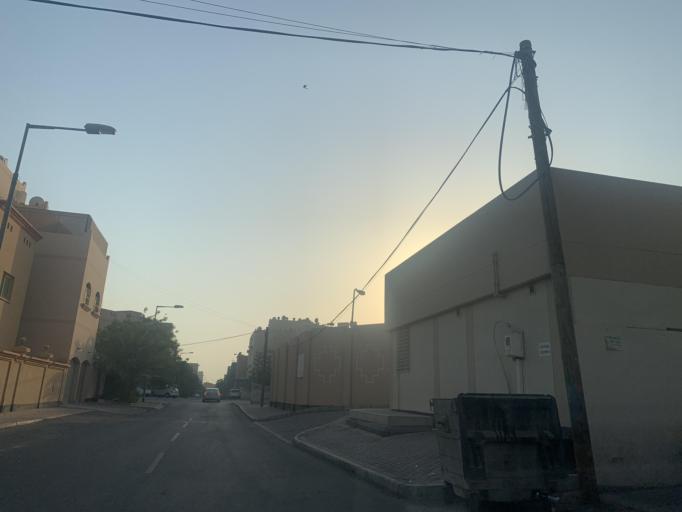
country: BH
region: Manama
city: Jidd Hafs
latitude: 26.2124
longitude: 50.5279
